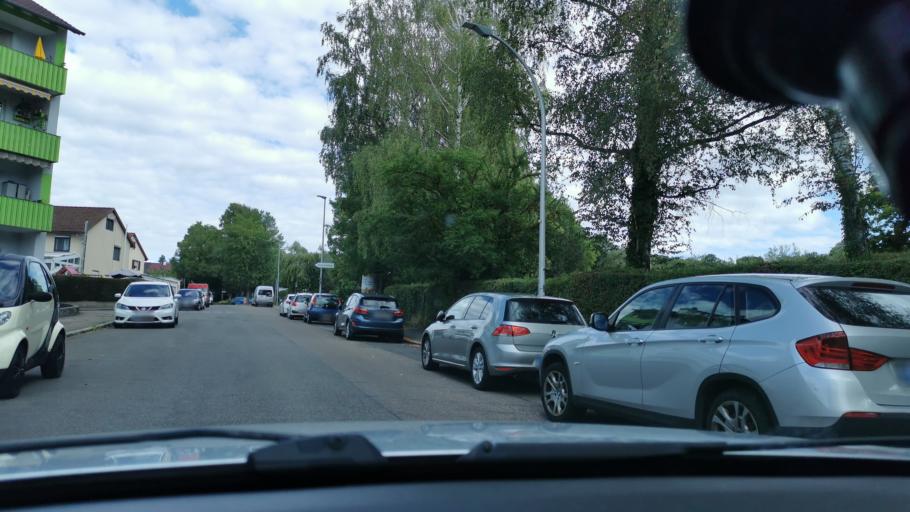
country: DE
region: Baden-Wuerttemberg
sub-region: Regierungsbezirk Stuttgart
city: Goeppingen
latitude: 48.7104
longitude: 9.6392
